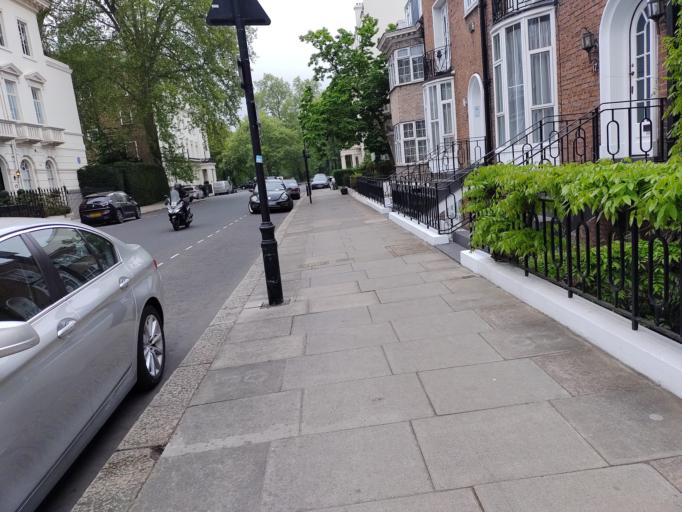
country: GB
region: England
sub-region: Greater London
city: Bayswater
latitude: 51.5134
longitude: -0.1680
